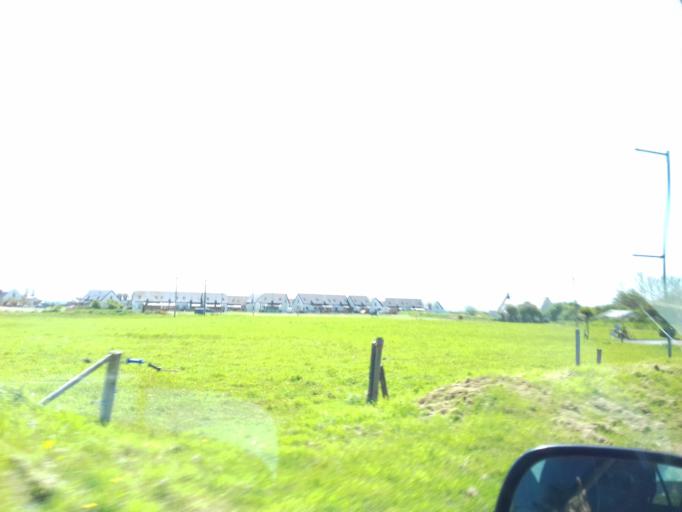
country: IE
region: Munster
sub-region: Waterford
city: Dunmore East
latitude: 52.1664
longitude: -6.8846
